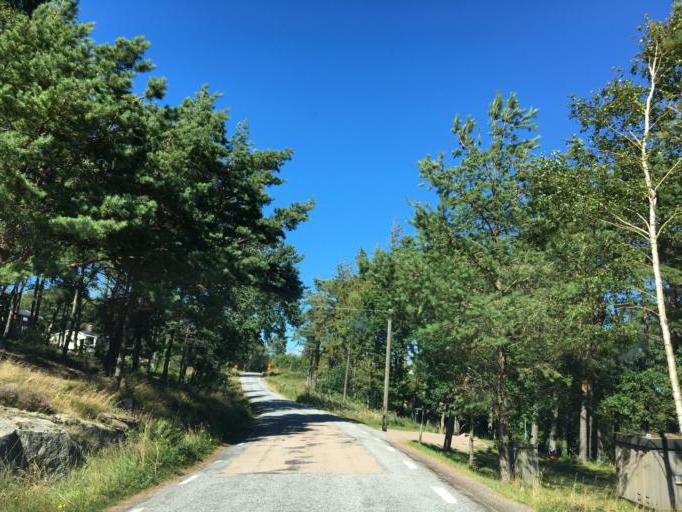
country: SE
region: Vaestra Goetaland
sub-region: Sotenas Kommun
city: Hunnebostrand
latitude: 58.4339
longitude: 11.2666
